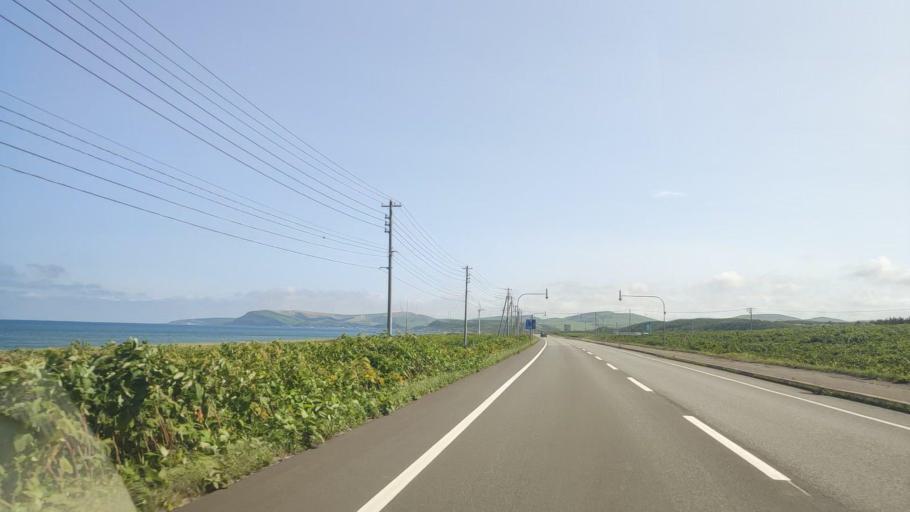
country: JP
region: Hokkaido
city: Makubetsu
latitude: 45.4255
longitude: 141.8457
